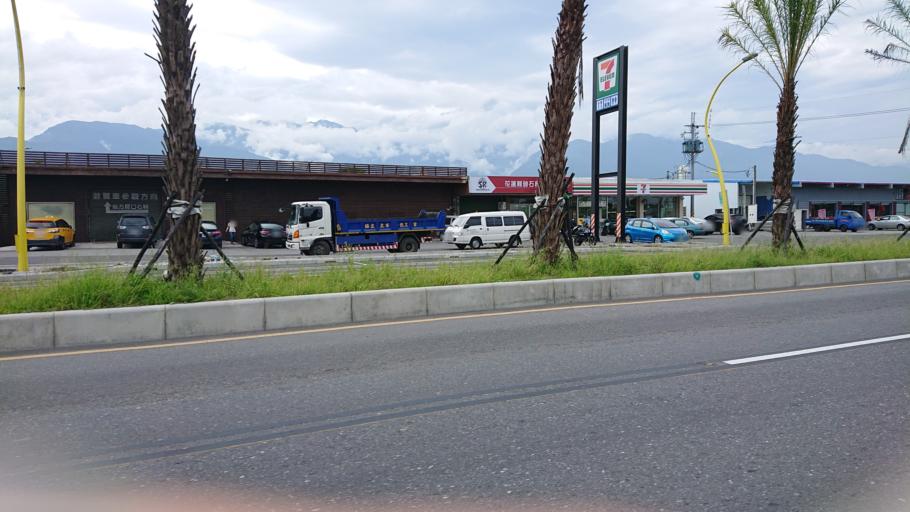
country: TW
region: Taiwan
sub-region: Hualien
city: Hualian
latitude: 23.9553
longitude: 121.6015
